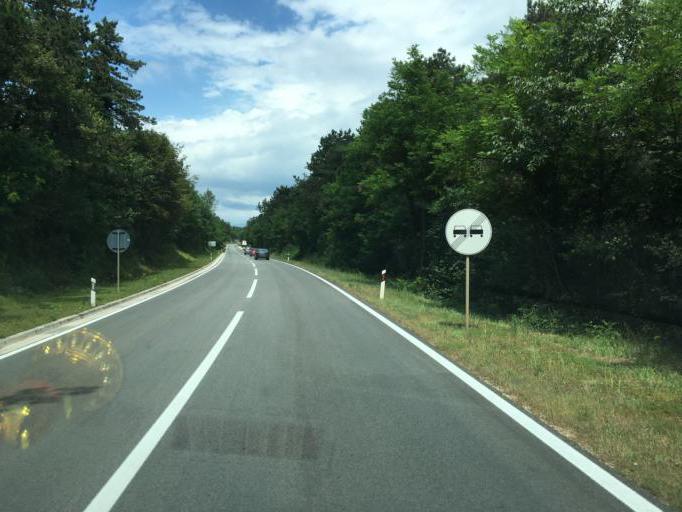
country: HR
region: Istarska
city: Karojba
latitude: 45.2243
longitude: 13.8399
